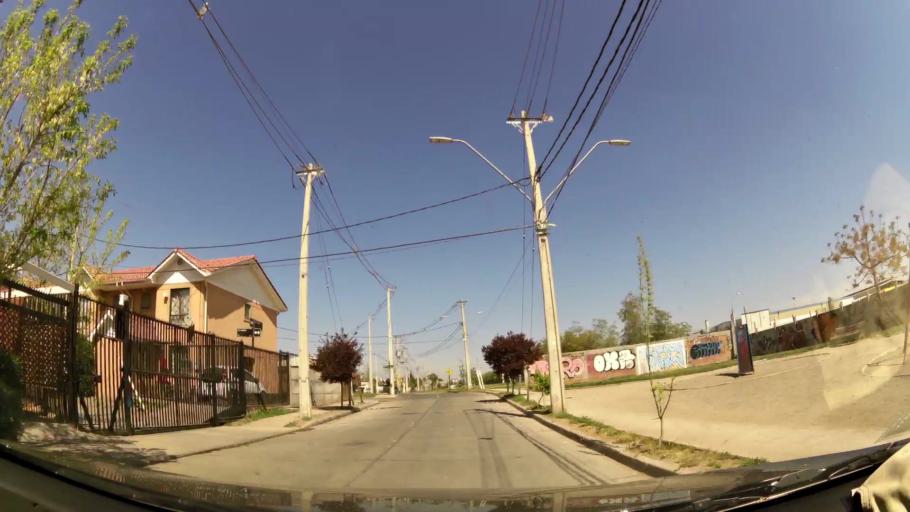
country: CL
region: Santiago Metropolitan
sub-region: Provincia de Santiago
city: Lo Prado
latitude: -33.3961
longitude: -70.7561
